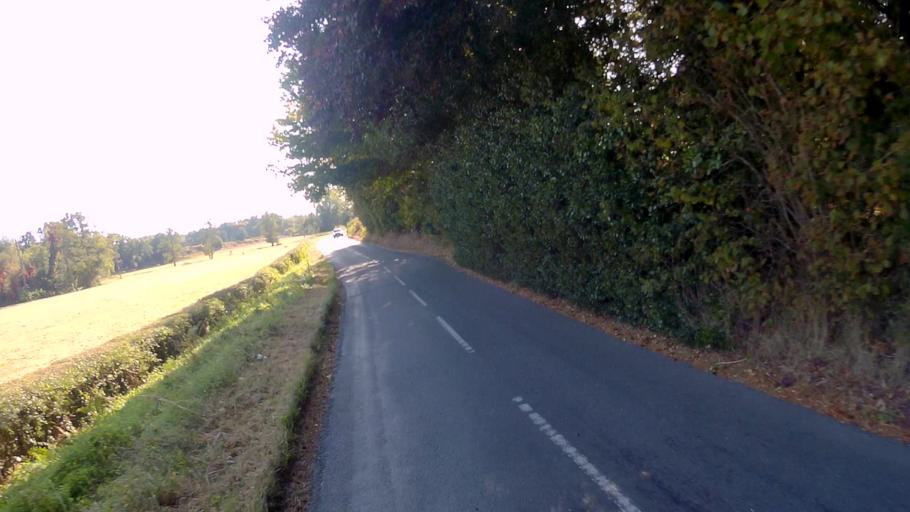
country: GB
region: England
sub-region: Surrey
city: Churt
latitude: 51.1671
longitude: -0.8023
